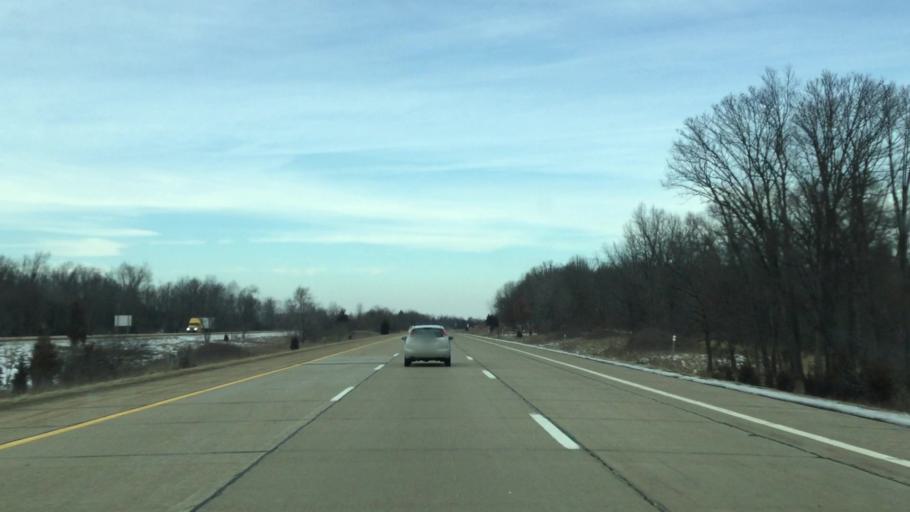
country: US
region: Michigan
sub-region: Calhoun County
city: Marshall
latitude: 42.3552
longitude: -84.9810
